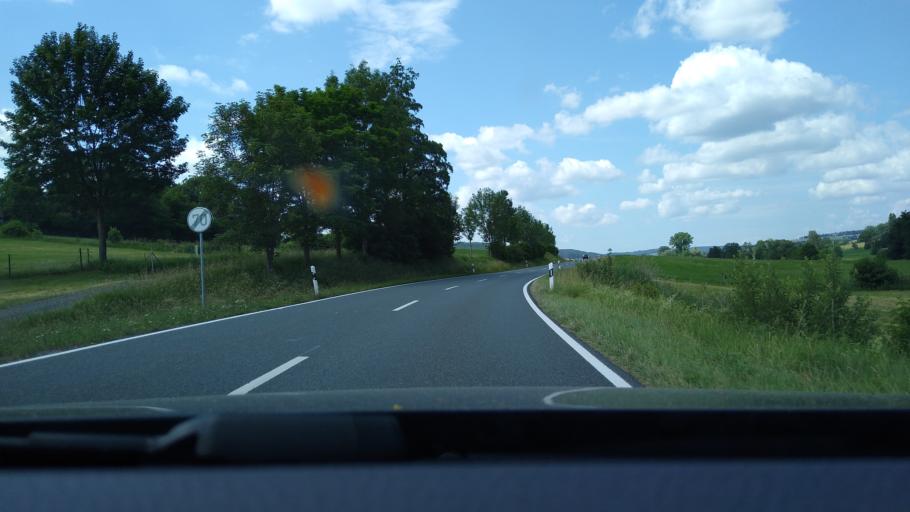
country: DE
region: Bavaria
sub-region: Regierungsbezirk Mittelfranken
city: Adelsdorf
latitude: 49.4704
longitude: 10.6827
